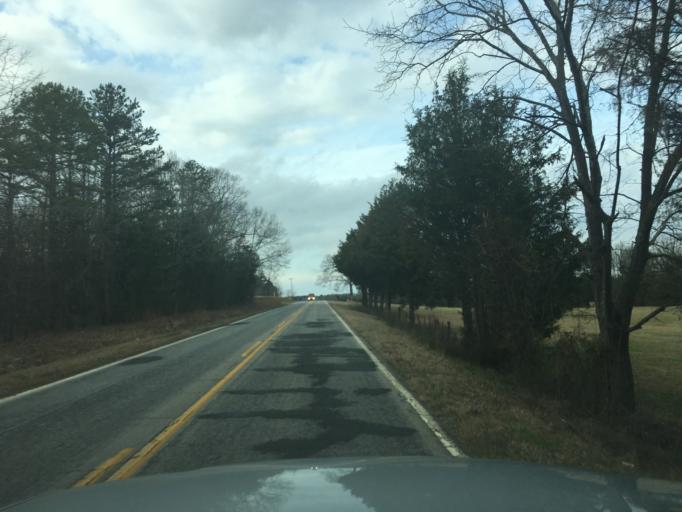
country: US
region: South Carolina
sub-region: Abbeville County
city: Due West
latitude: 34.3169
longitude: -82.4636
